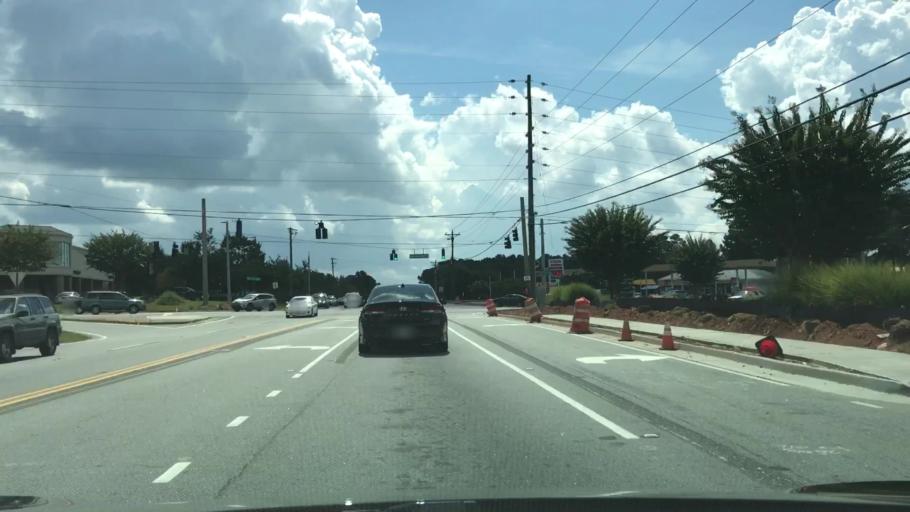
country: US
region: Georgia
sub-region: Gwinnett County
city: Snellville
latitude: 33.8873
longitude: -84.0605
